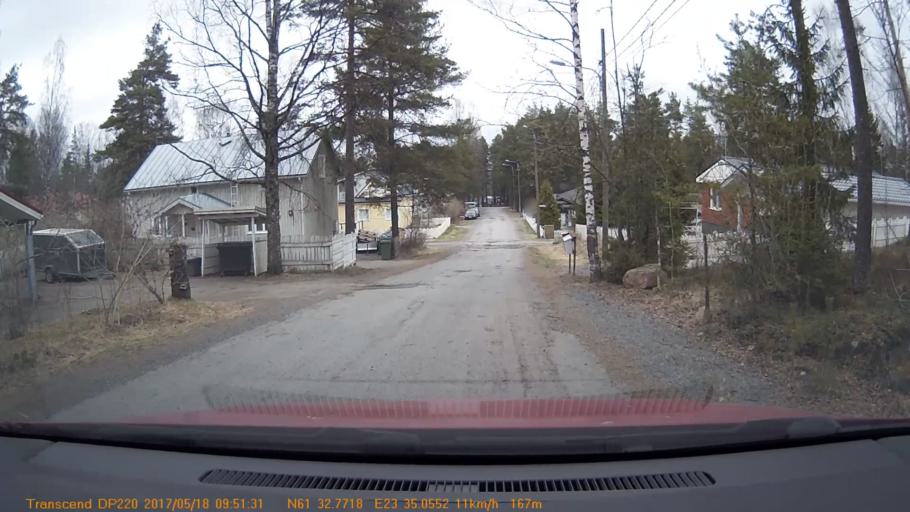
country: FI
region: Pirkanmaa
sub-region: Tampere
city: Yloejaervi
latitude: 61.5463
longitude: 23.5844
